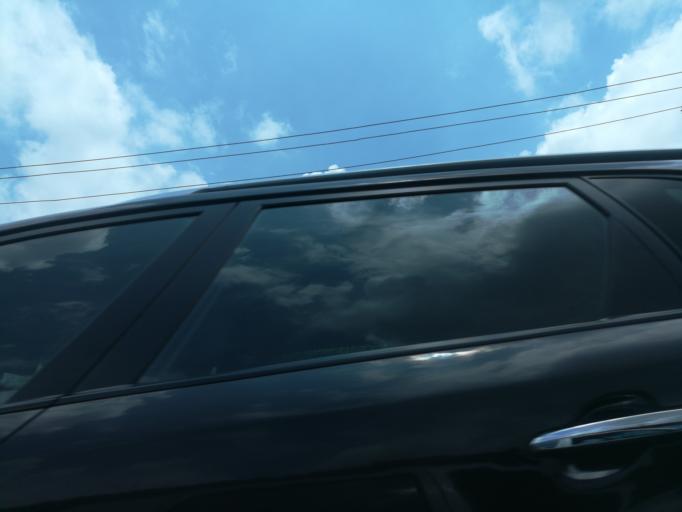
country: NG
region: Lagos
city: Oshodi
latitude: 6.5560
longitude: 3.3576
